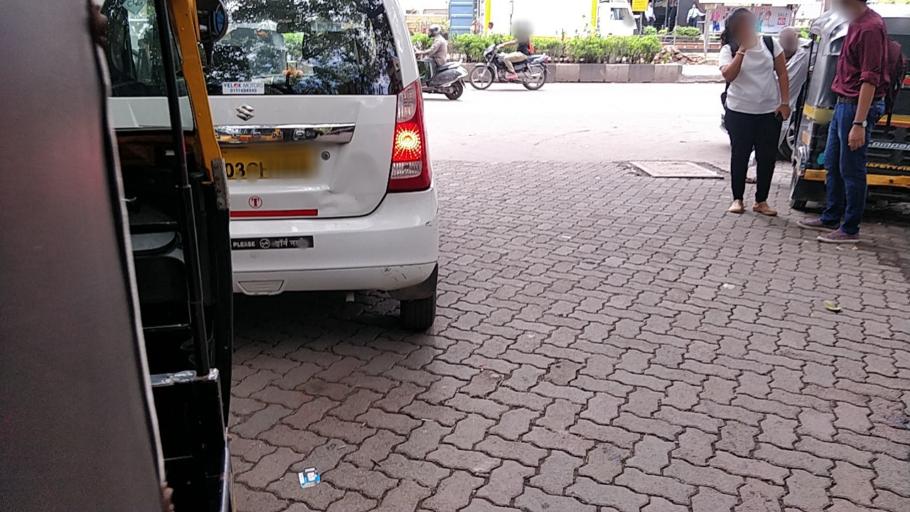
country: IN
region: Maharashtra
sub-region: Mumbai Suburban
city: Mumbai
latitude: 19.0610
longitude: 72.8360
